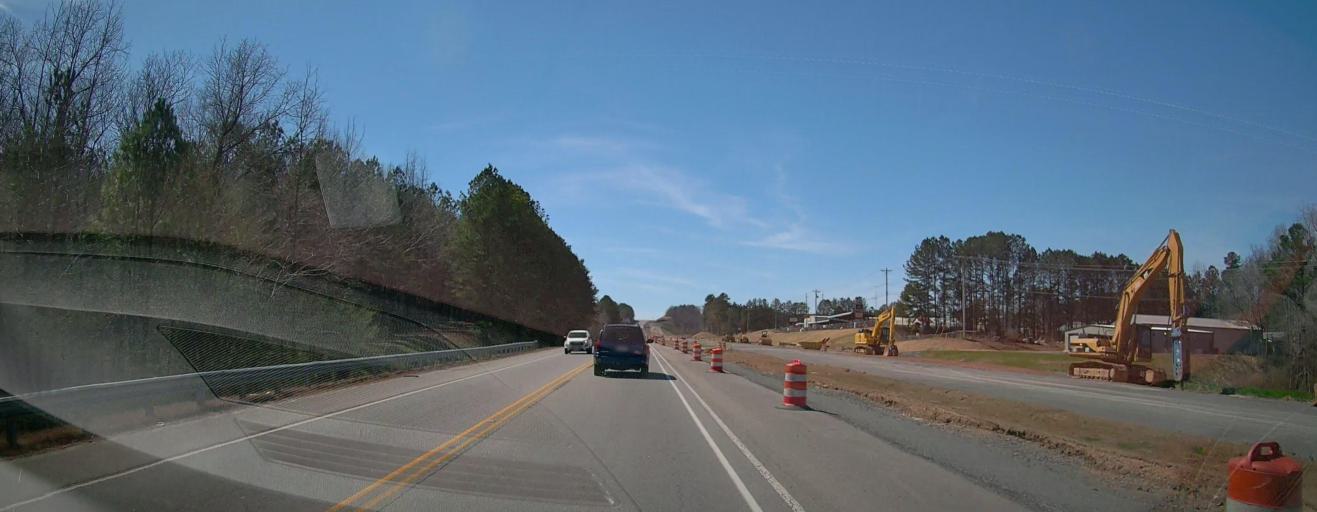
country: US
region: Alabama
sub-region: Cullman County
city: Cullman
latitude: 34.2058
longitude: -86.8399
